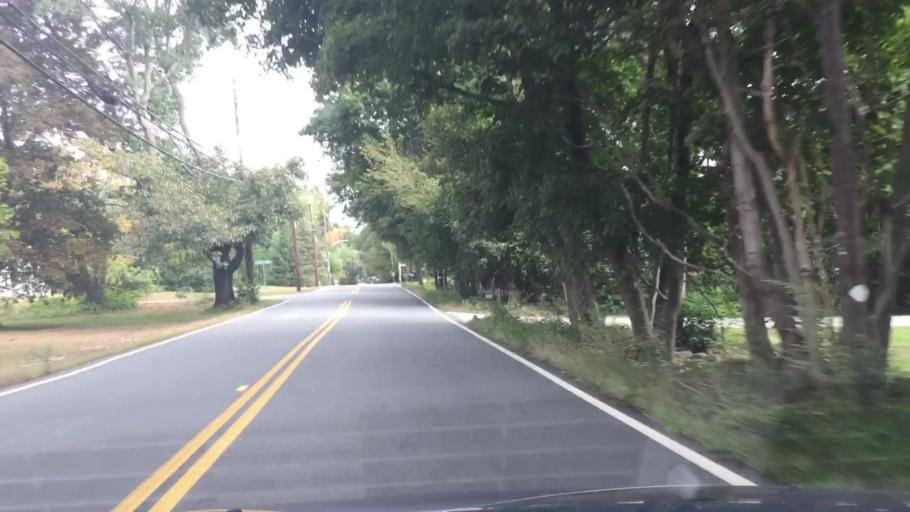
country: US
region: Massachusetts
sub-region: Essex County
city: Methuen
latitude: 42.6745
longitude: -71.2264
